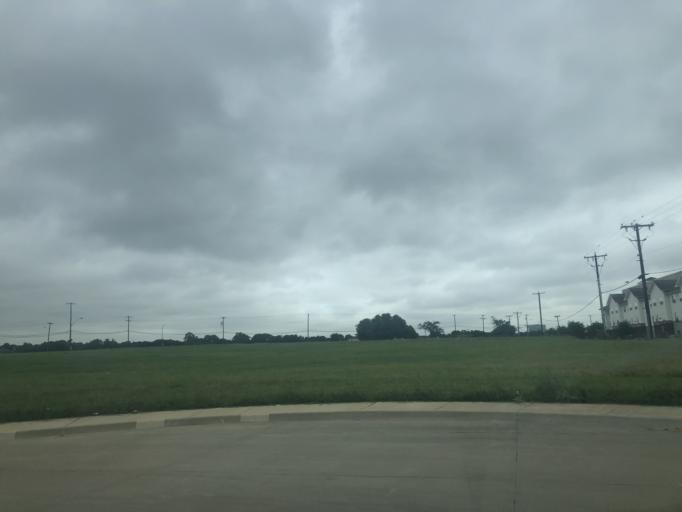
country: US
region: Texas
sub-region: Dallas County
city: Cockrell Hill
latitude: 32.7838
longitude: -96.8637
